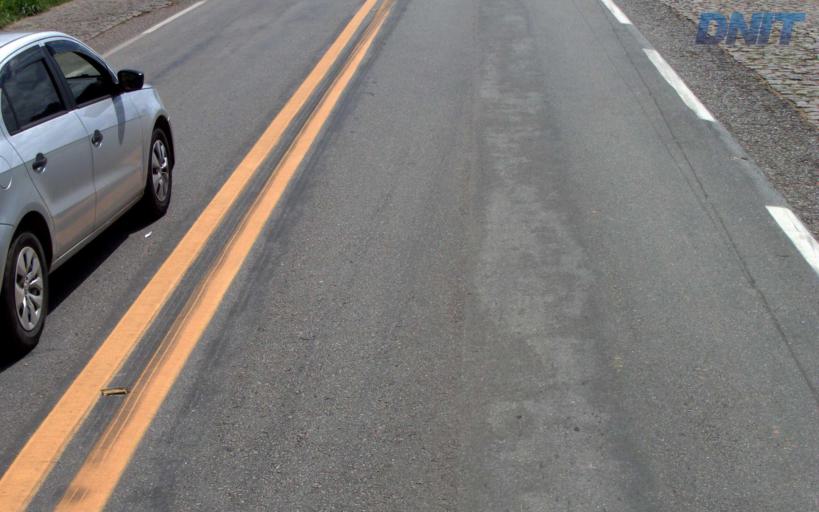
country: BR
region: Minas Gerais
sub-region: Governador Valadares
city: Governador Valadares
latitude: -19.0481
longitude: -42.1555
